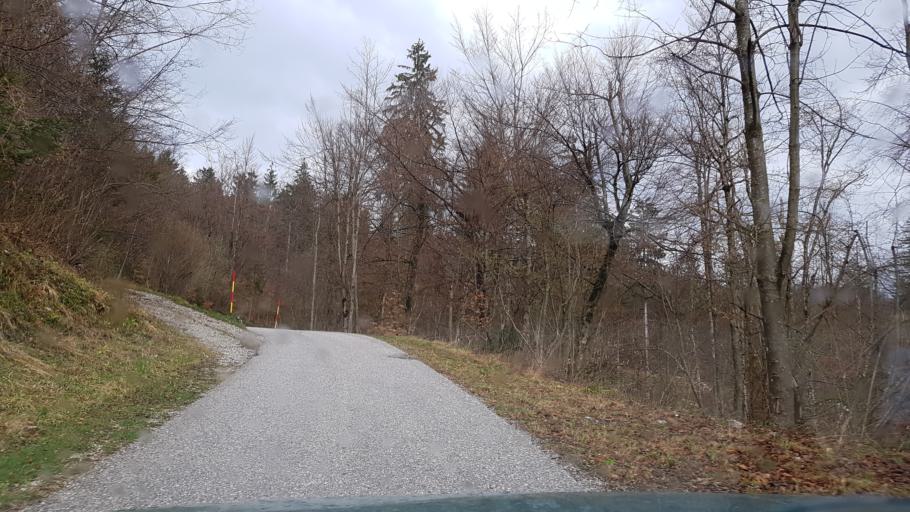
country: SI
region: Cerkno
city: Cerkno
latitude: 46.1262
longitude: 13.8630
